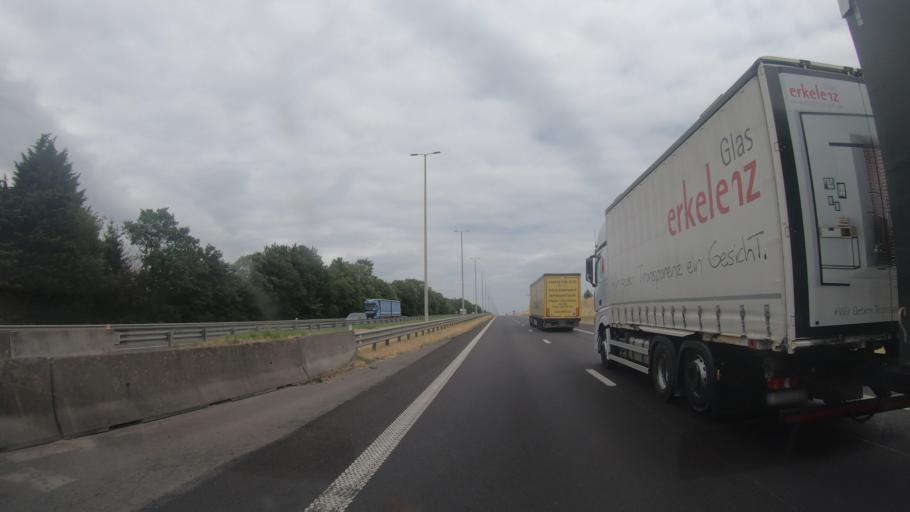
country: BE
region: Wallonia
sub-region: Province de Liege
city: Dison
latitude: 50.6394
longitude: 5.8536
